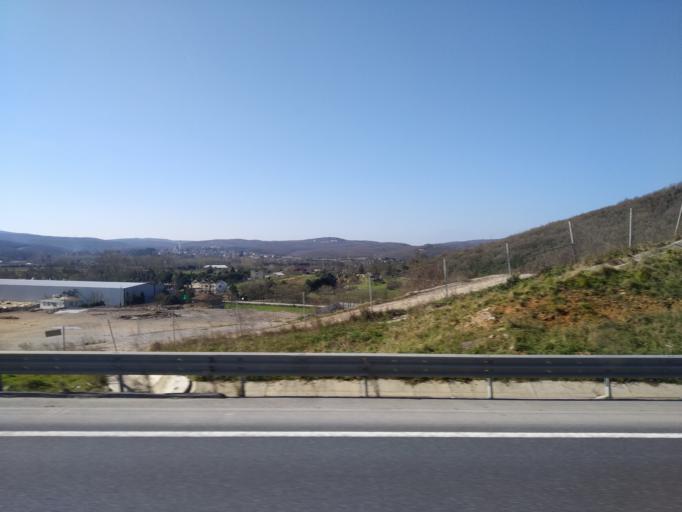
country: TR
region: Istanbul
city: Mahmut Sevket Pasa
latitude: 41.1333
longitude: 29.2867
